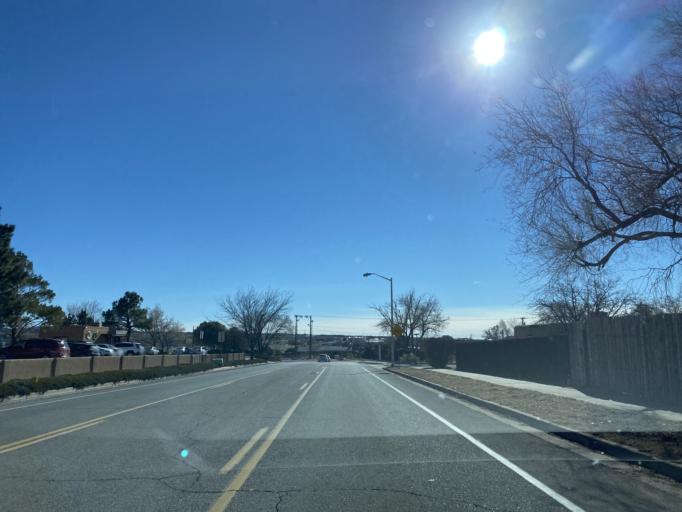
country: US
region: New Mexico
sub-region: Santa Fe County
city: Santa Fe
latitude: 35.6532
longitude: -105.9585
